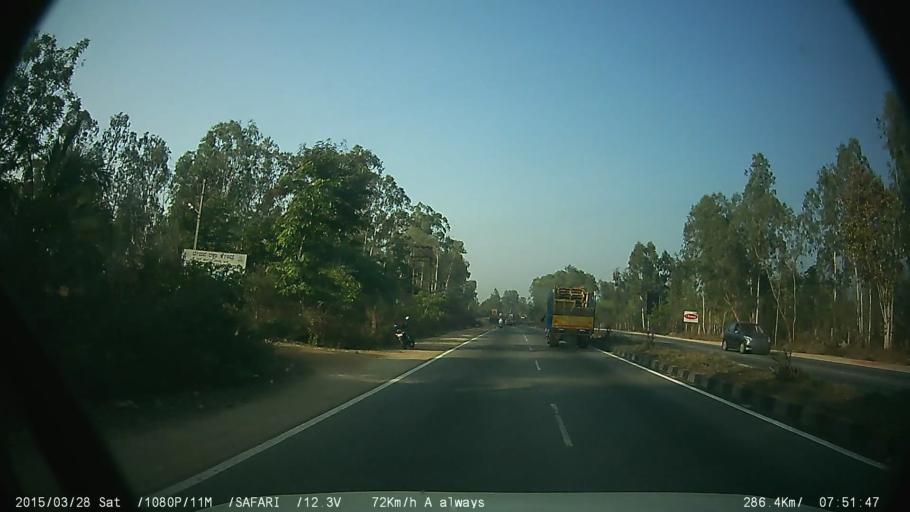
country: IN
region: Karnataka
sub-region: Mandya
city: Shrirangapattana
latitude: 12.4582
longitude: 76.7440
